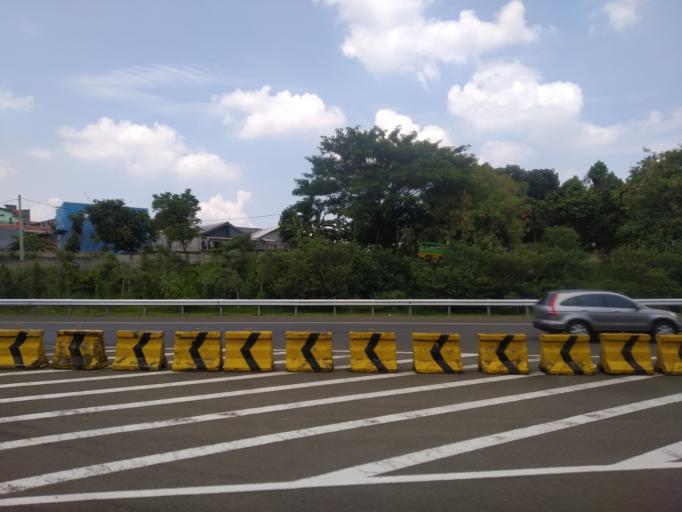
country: ID
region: West Java
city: Bogor
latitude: -6.5989
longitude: 106.8152
